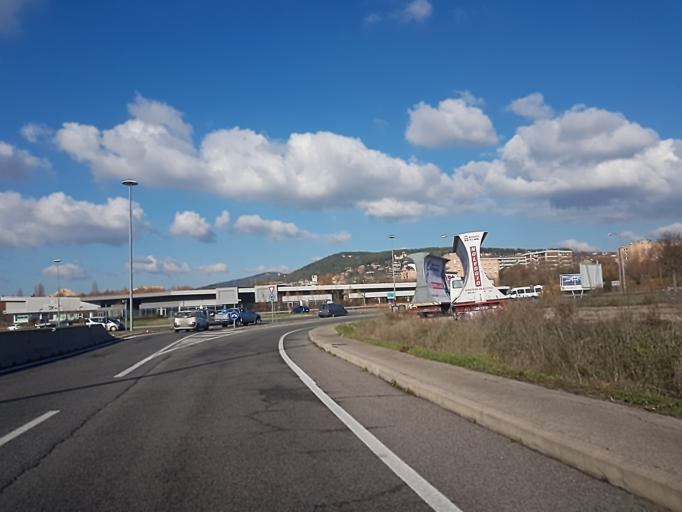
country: IT
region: Umbria
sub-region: Provincia di Perugia
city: Lacugnano
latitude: 43.0781
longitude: 12.3472
